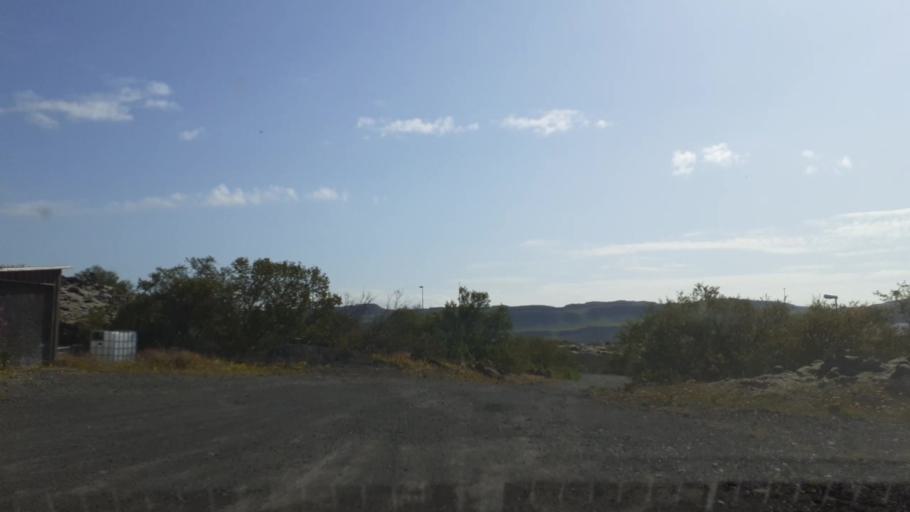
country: IS
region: West
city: Borgarnes
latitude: 64.7678
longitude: -21.5490
